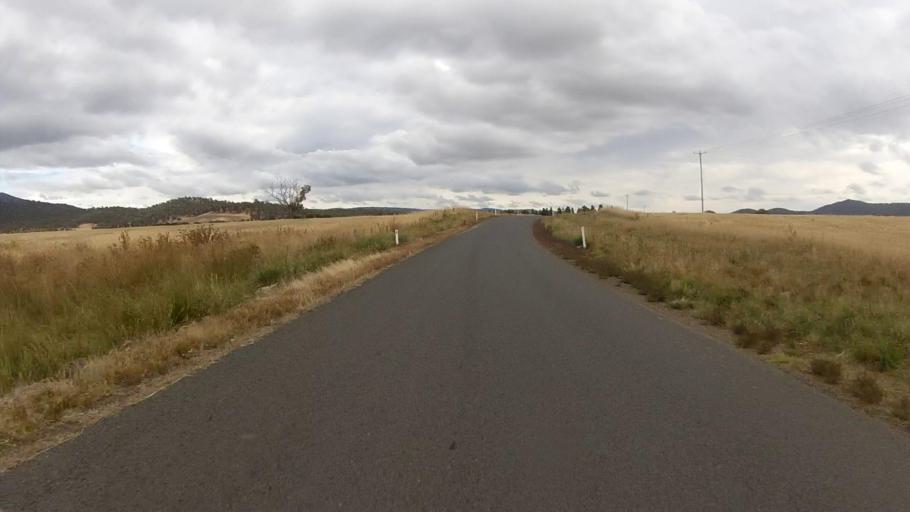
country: AU
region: Tasmania
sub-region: Break O'Day
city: St Helens
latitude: -41.8248
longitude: 147.8429
